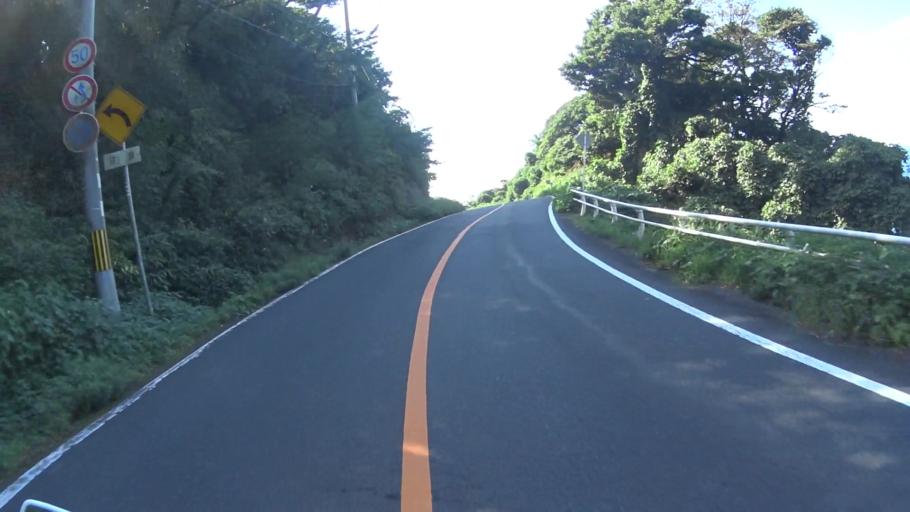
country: JP
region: Kyoto
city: Miyazu
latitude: 35.7460
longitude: 135.1295
